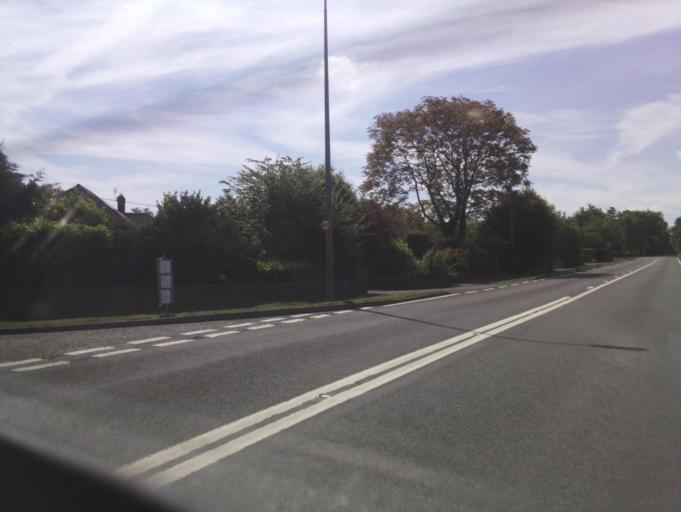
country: GB
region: England
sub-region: North Lincolnshire
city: Manton
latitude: 53.5326
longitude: -0.5774
